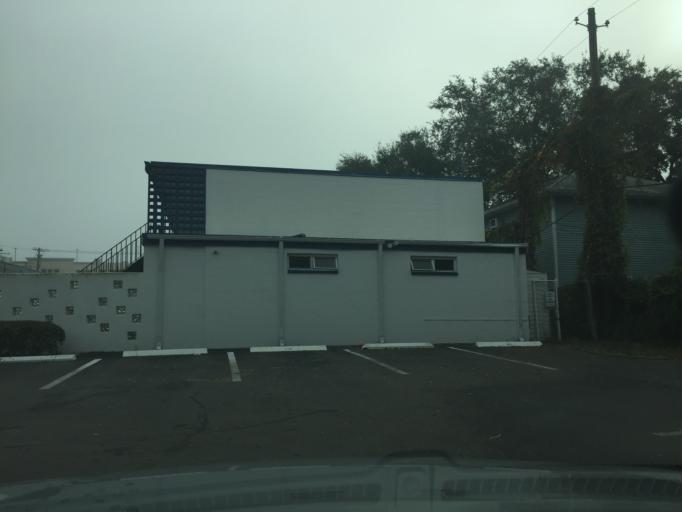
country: US
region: Florida
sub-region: Hillsborough County
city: Tampa
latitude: 27.9357
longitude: -82.4840
